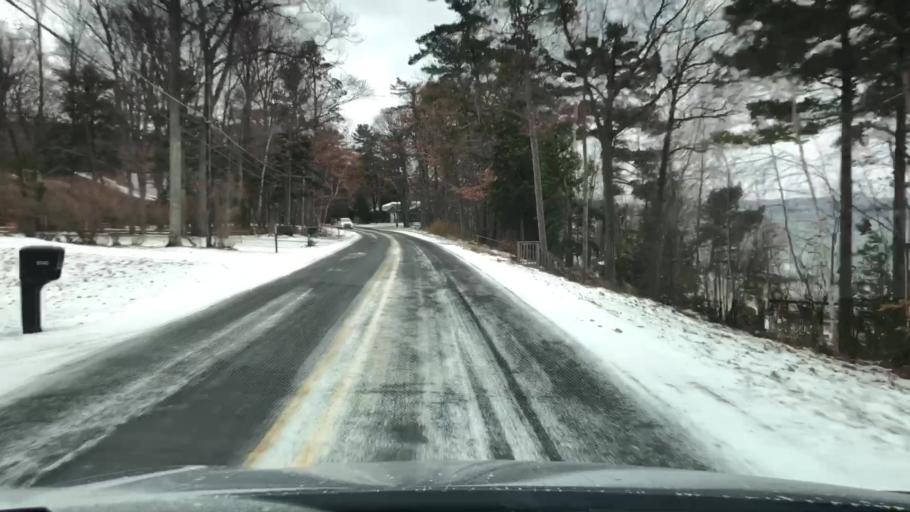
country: US
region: Michigan
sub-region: Grand Traverse County
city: Traverse City
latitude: 44.8289
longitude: -85.5655
